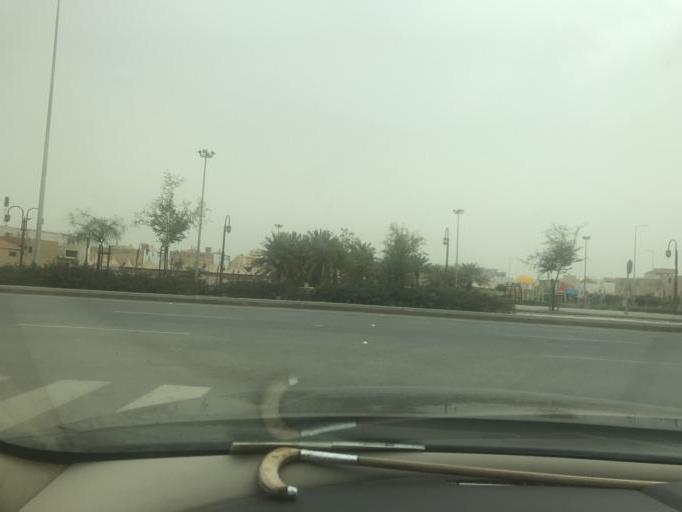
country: SA
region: Ar Riyad
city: Riyadh
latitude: 24.7267
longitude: 46.7895
